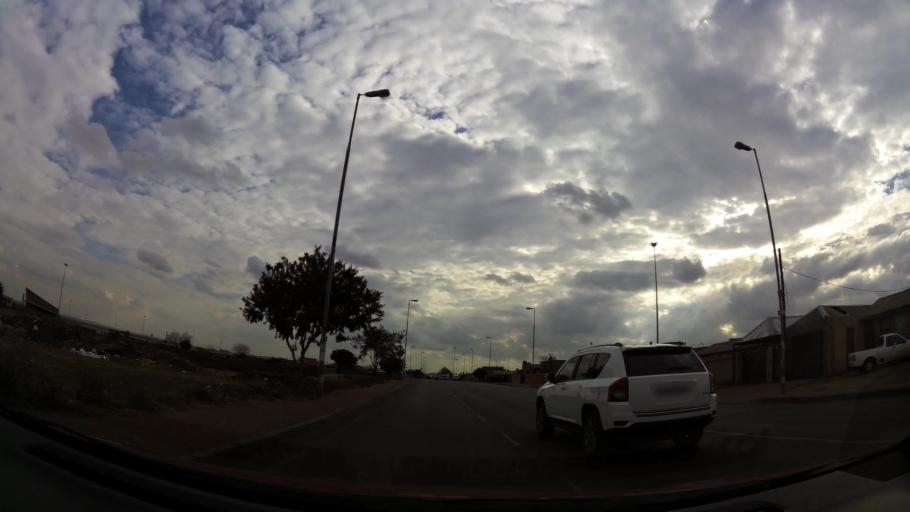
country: ZA
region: Gauteng
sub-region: City of Johannesburg Metropolitan Municipality
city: Soweto
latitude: -26.2488
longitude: 27.8200
